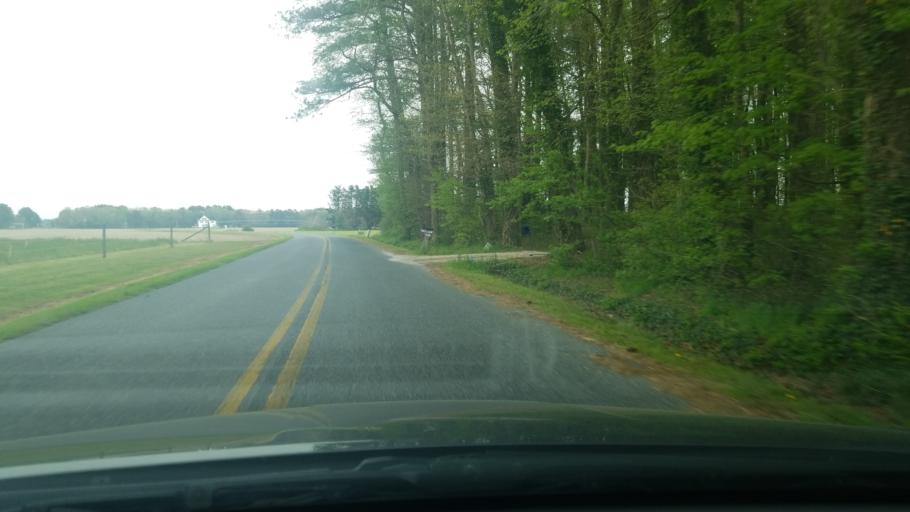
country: US
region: Maryland
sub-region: Worcester County
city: Snow Hill
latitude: 38.2364
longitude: -75.3089
